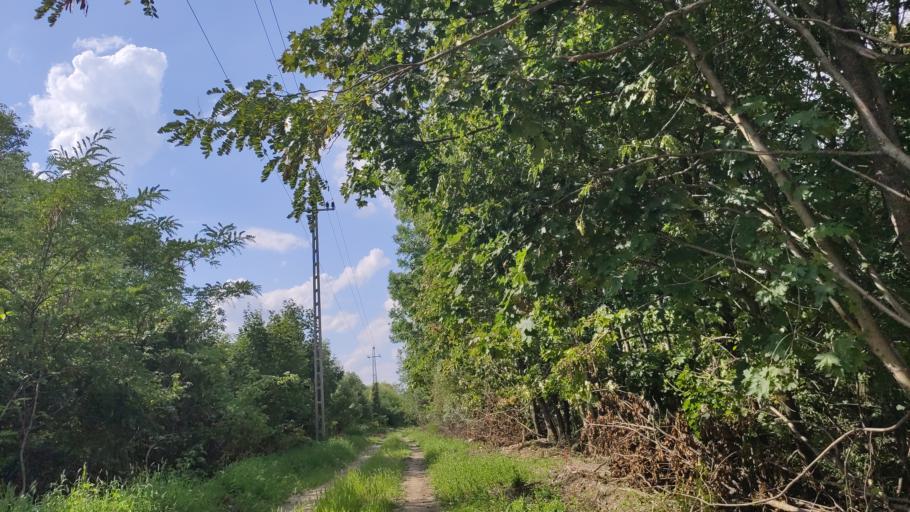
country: HU
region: Pest
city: Biatorbagy
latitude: 47.4634
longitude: 18.8702
